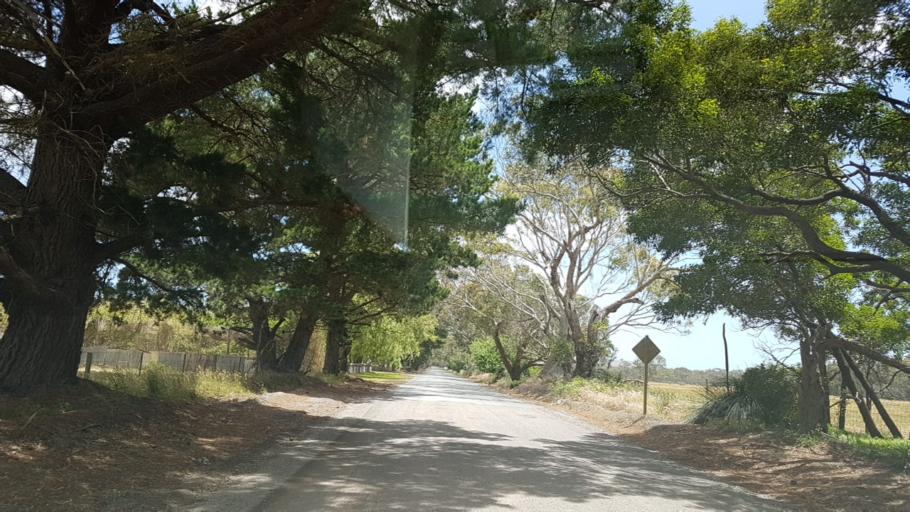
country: AU
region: South Australia
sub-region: Onkaparinga
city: Aldinga
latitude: -35.3771
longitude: 138.4960
